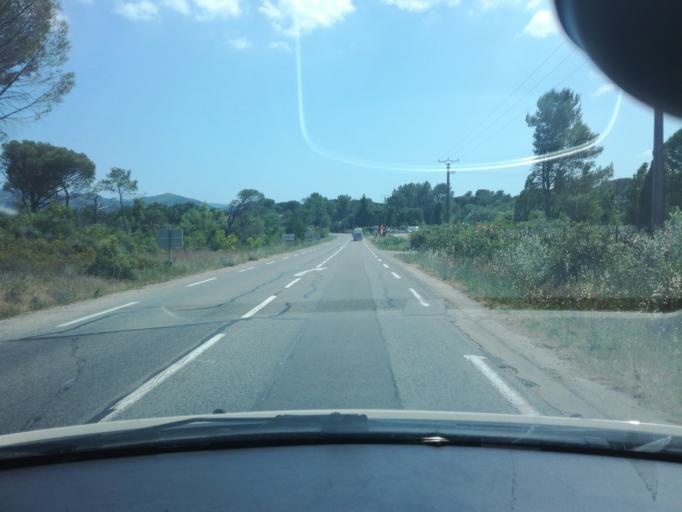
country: FR
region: Provence-Alpes-Cote d'Azur
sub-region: Departement du Var
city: Le Muy
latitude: 43.4907
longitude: 6.5652
